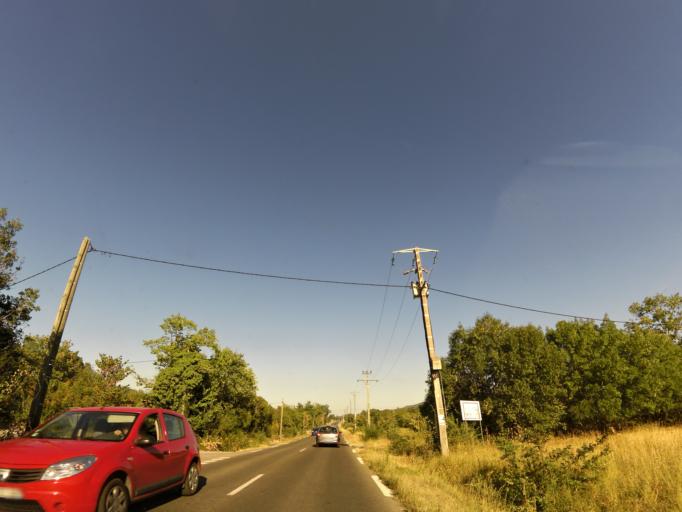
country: FR
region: Languedoc-Roussillon
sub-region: Departement du Gard
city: Saint-Hippolyte-du-Fort
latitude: 43.9485
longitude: 3.8969
